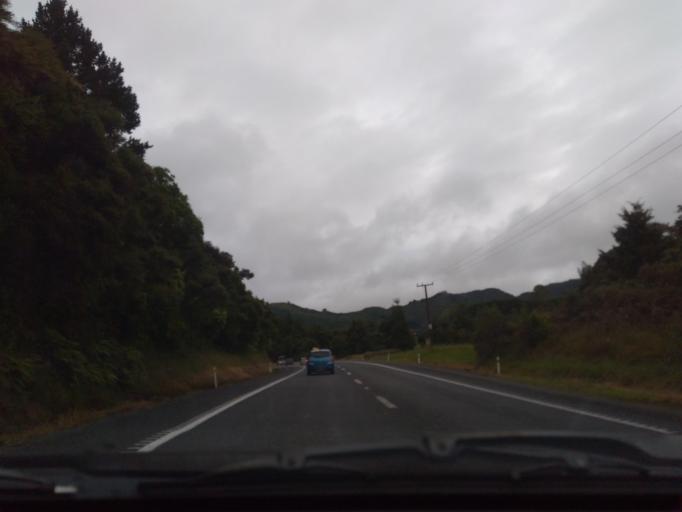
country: NZ
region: Auckland
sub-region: Auckland
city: Wellsford
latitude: -36.1115
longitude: 174.4338
